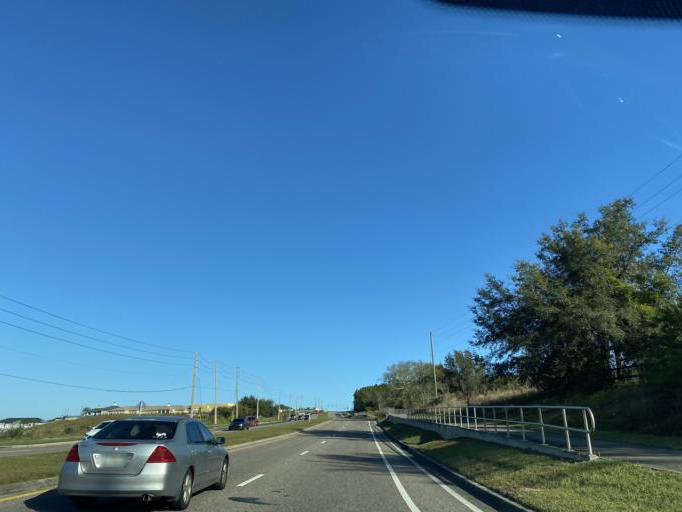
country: US
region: Florida
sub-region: Lake County
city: Minneola
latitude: 28.5379
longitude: -81.7235
